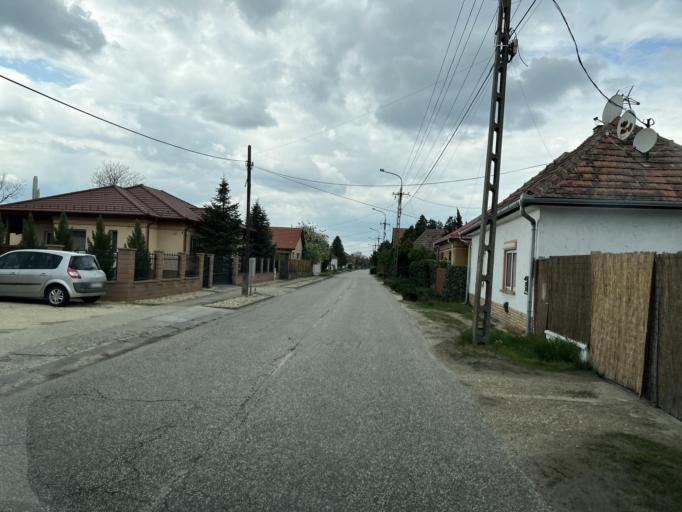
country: HU
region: Pest
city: Hernad
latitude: 47.1636
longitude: 19.4309
